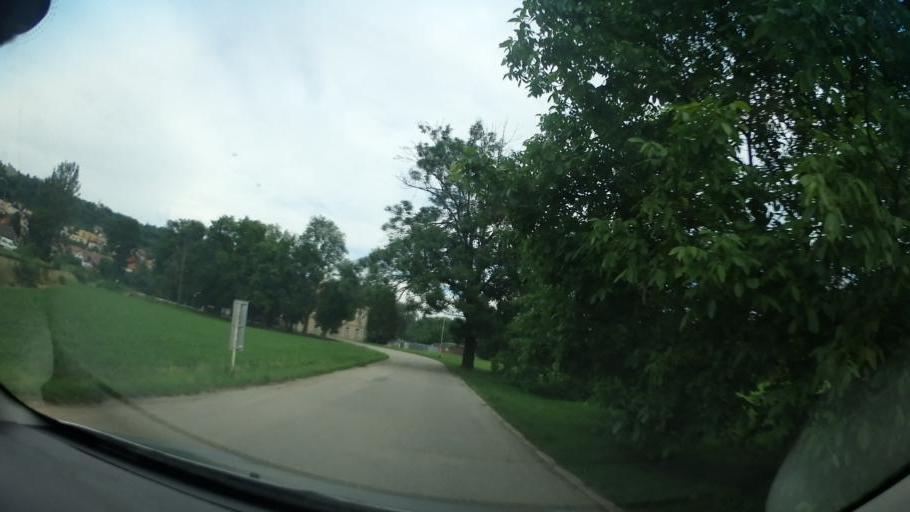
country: CZ
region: South Moravian
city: Ivancice
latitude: 49.0998
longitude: 16.3858
